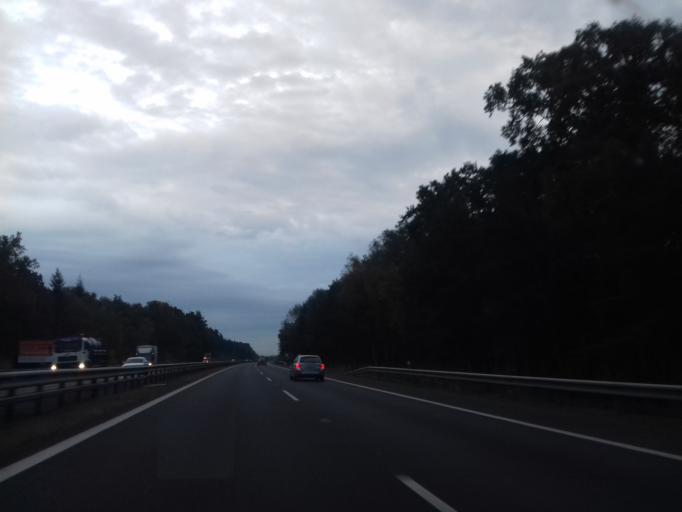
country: CZ
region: Central Bohemia
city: Poricany
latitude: 50.1244
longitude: 14.9237
